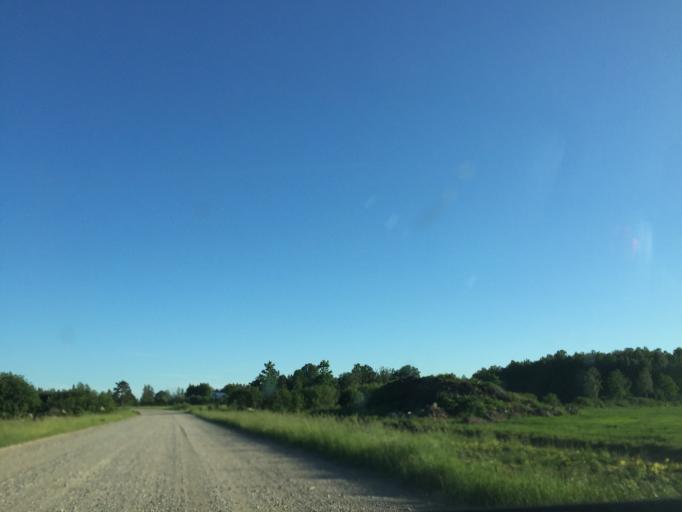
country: LV
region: Broceni
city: Broceni
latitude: 56.8429
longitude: 22.5660
